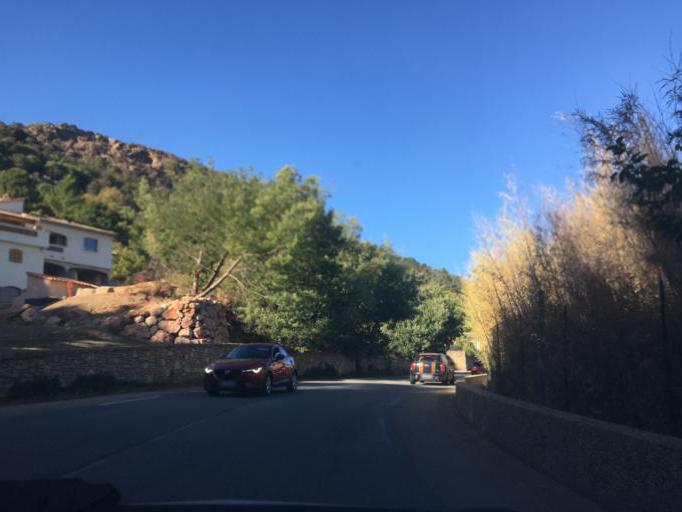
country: FR
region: Provence-Alpes-Cote d'Azur
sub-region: Departement du Var
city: La Garde-Freinet
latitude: 43.3063
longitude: 6.4686
